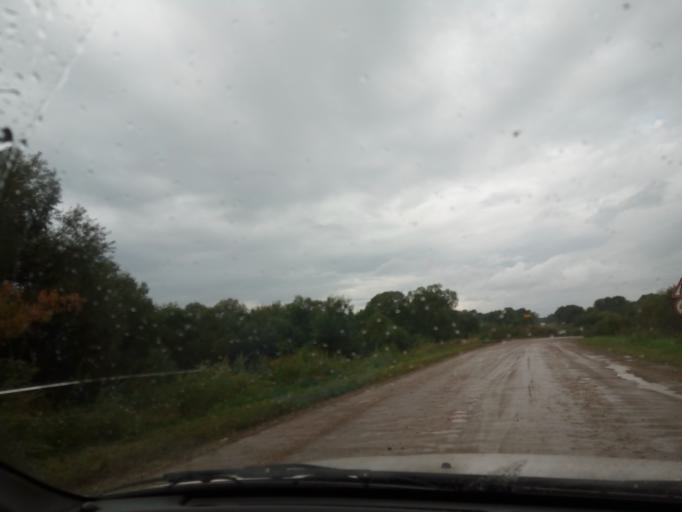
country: RU
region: Primorskiy
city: Lazo
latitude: 45.8520
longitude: 133.6460
